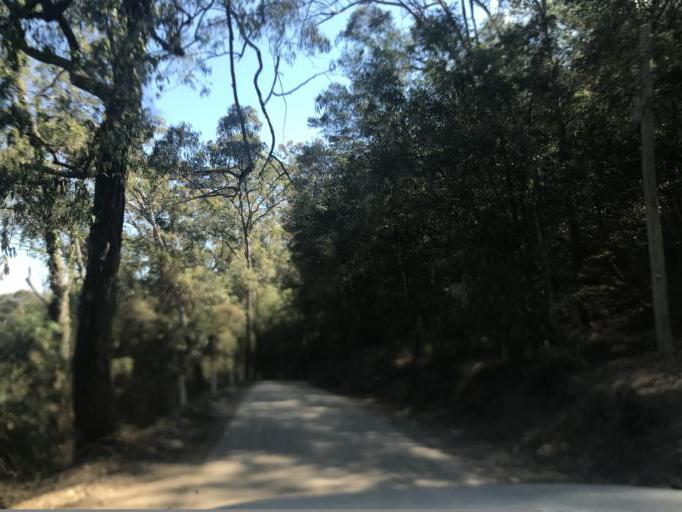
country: AU
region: New South Wales
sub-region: Hawkesbury
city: Pitt Town
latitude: -33.4179
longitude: 150.9077
